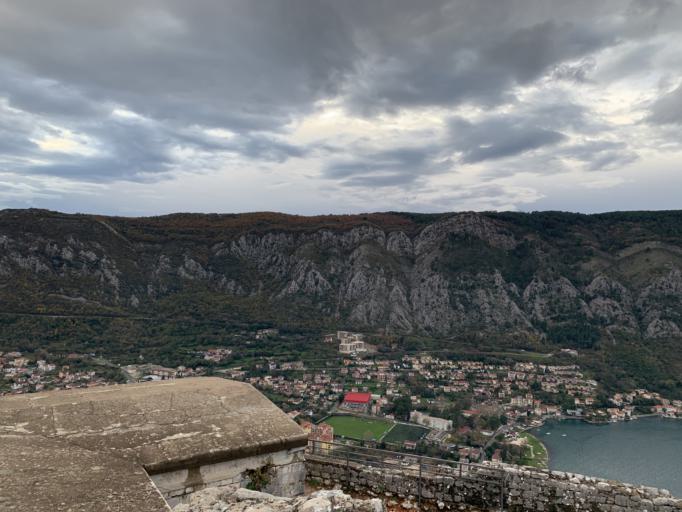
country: ME
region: Kotor
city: Kotor
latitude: 42.4220
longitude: 18.7749
